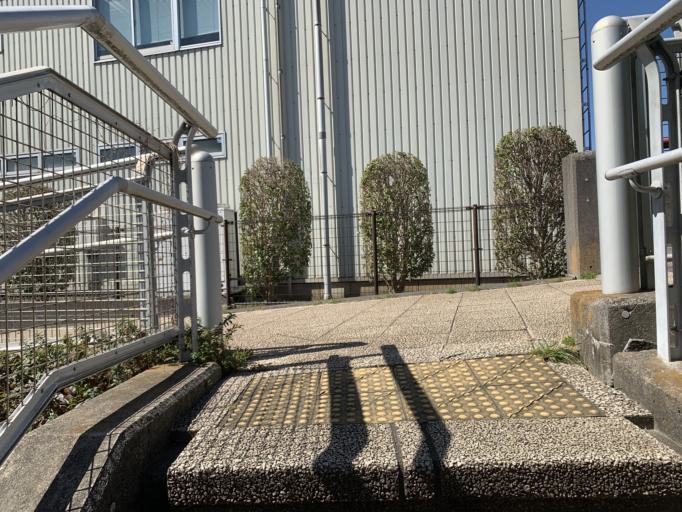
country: JP
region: Tokyo
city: Chofugaoka
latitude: 35.5542
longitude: 139.5849
